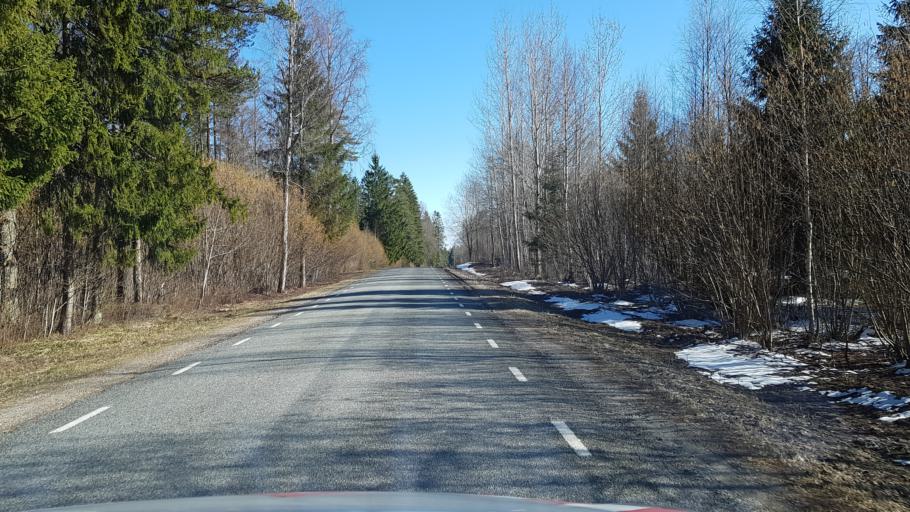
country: EE
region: Laeaene-Virumaa
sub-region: Kadrina vald
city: Kadrina
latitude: 59.3929
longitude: 26.0174
